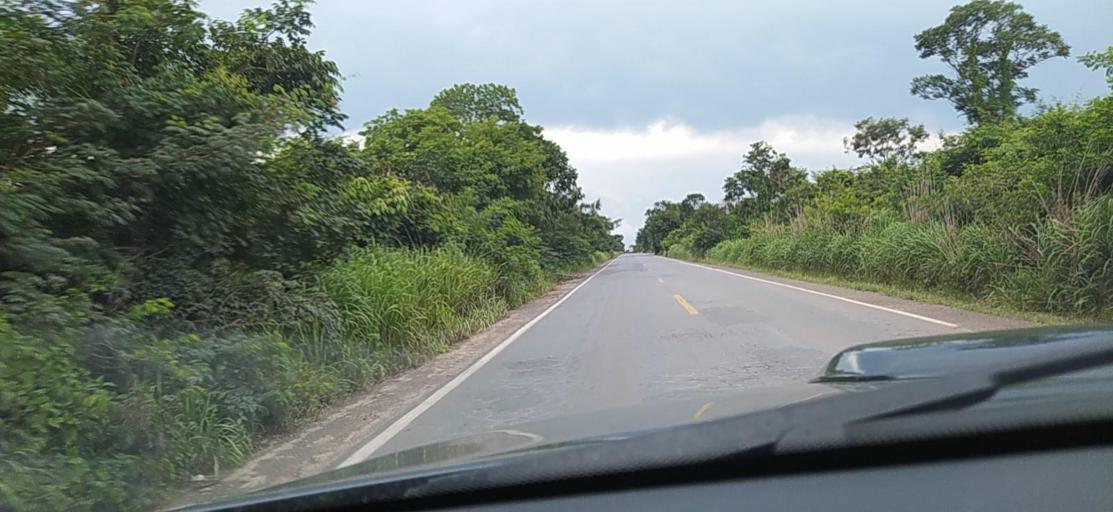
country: BR
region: Minas Gerais
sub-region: Francisco Sa
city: Francisco Sa
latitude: -16.2525
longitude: -43.6334
